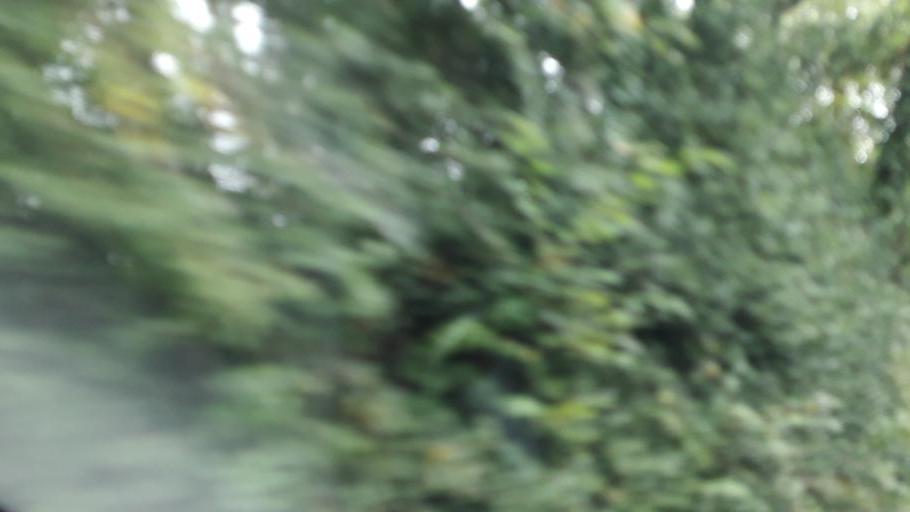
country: IE
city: Knocklyon
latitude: 53.2644
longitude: -6.3246
